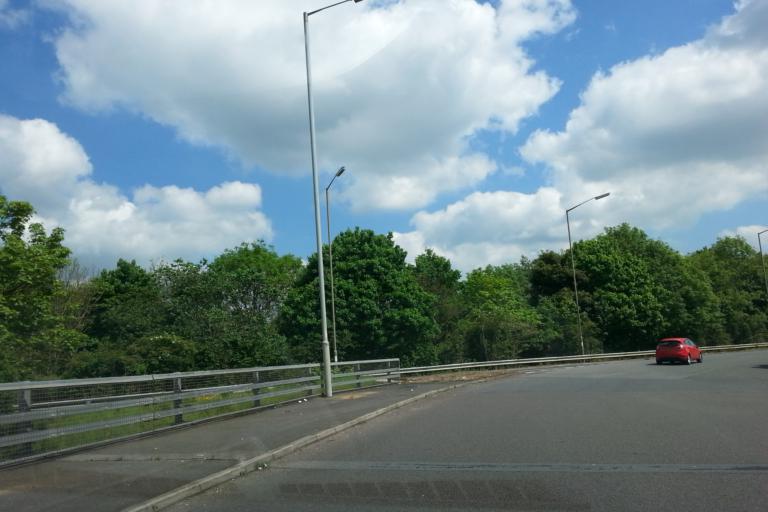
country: GB
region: England
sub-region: Peterborough
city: Peterborough
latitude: 52.5647
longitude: -0.2852
